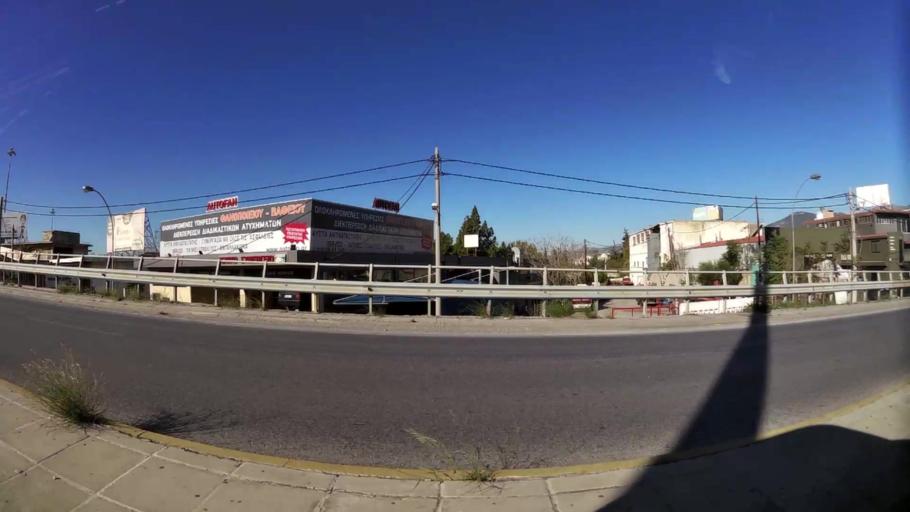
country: GR
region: Attica
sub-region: Nomarchia Athinas
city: Metamorfosi
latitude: 38.0701
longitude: 23.7601
